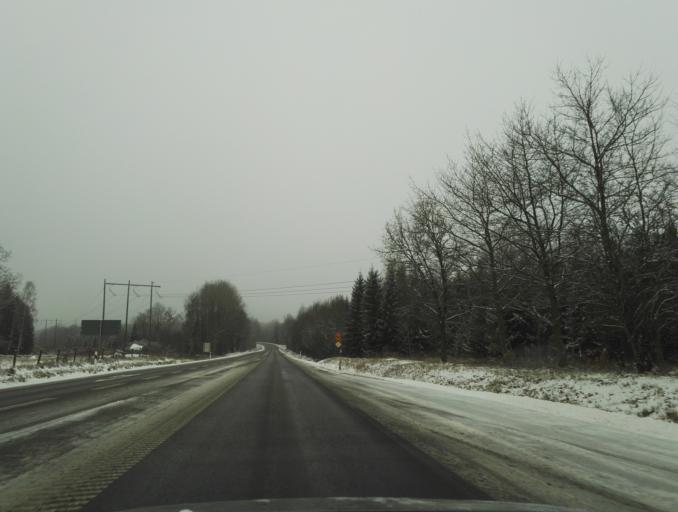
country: SE
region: Kronoberg
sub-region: Vaxjo Kommun
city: Vaexjoe
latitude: 56.8663
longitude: 14.7365
